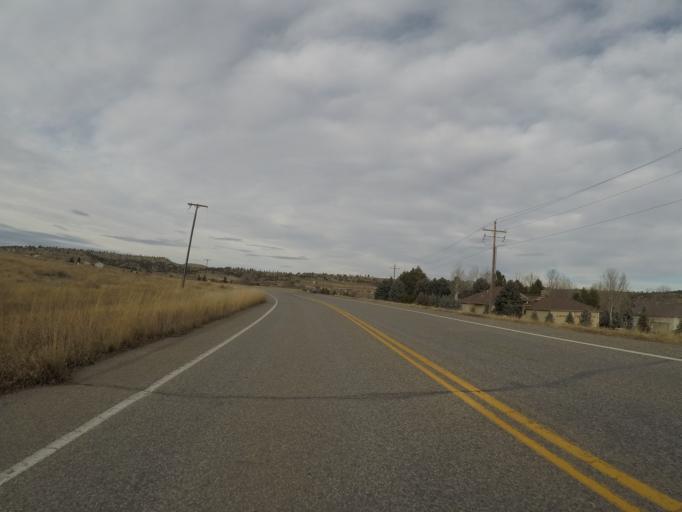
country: US
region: Montana
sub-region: Yellowstone County
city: Laurel
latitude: 45.8084
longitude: -108.6737
